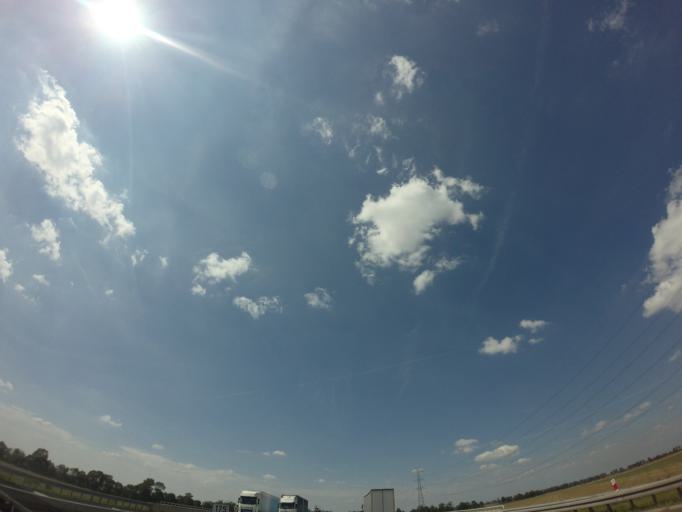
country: PL
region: Lower Silesian Voivodeship
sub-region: Powiat olawski
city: Wierzbno
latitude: 50.9035
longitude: 17.1656
